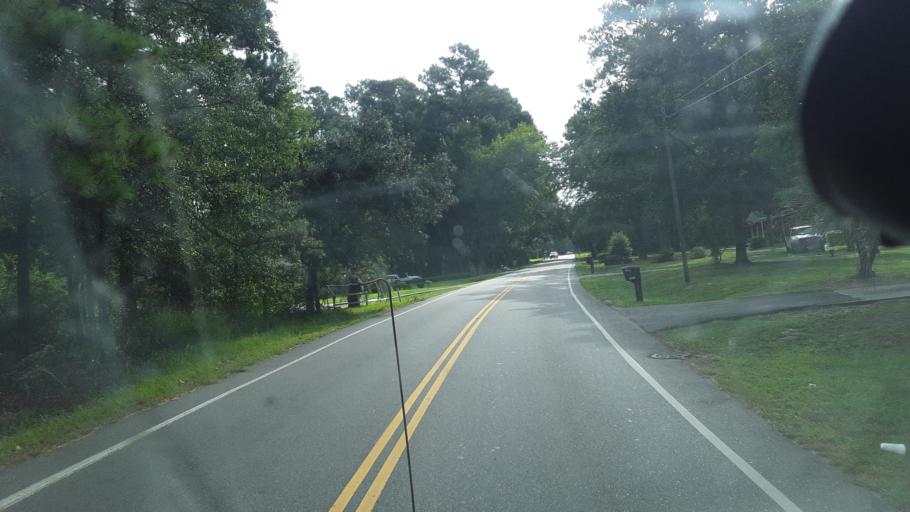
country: US
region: South Carolina
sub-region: Horry County
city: Conway
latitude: 33.8229
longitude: -79.0806
